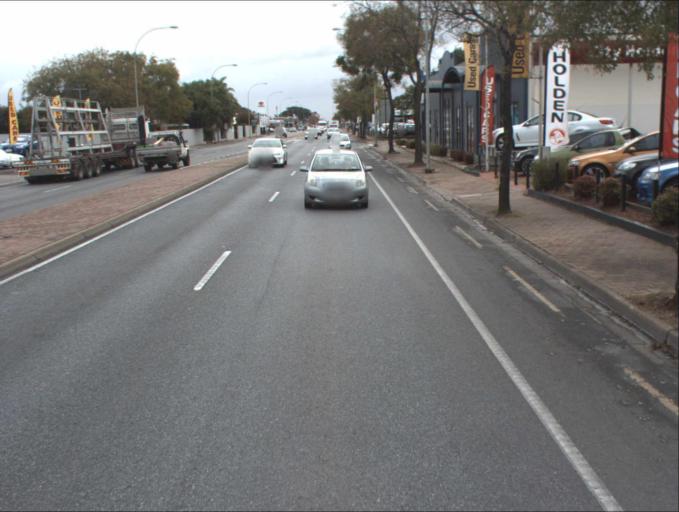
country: AU
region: South Australia
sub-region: Prospect
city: Prospect
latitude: -34.8867
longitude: 138.6029
